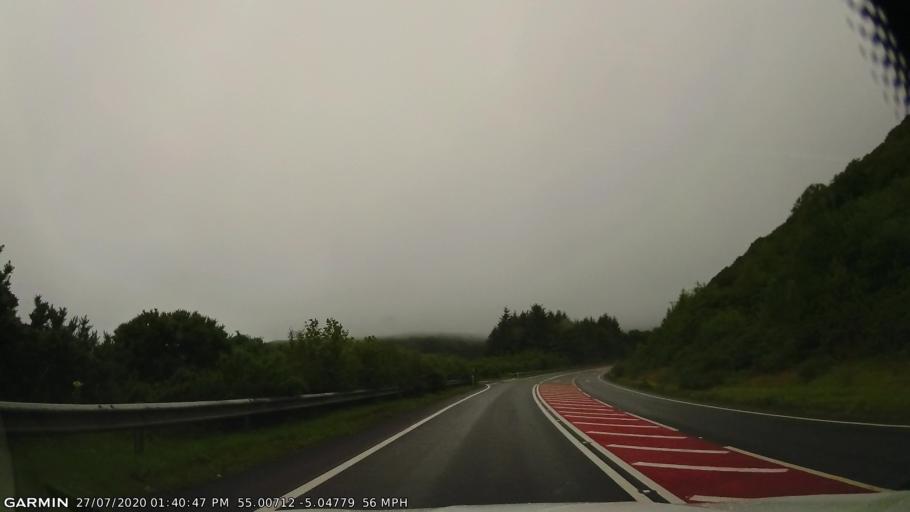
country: GB
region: Scotland
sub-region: Dumfries and Galloway
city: Cairnryan
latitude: 55.0071
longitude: -5.0478
